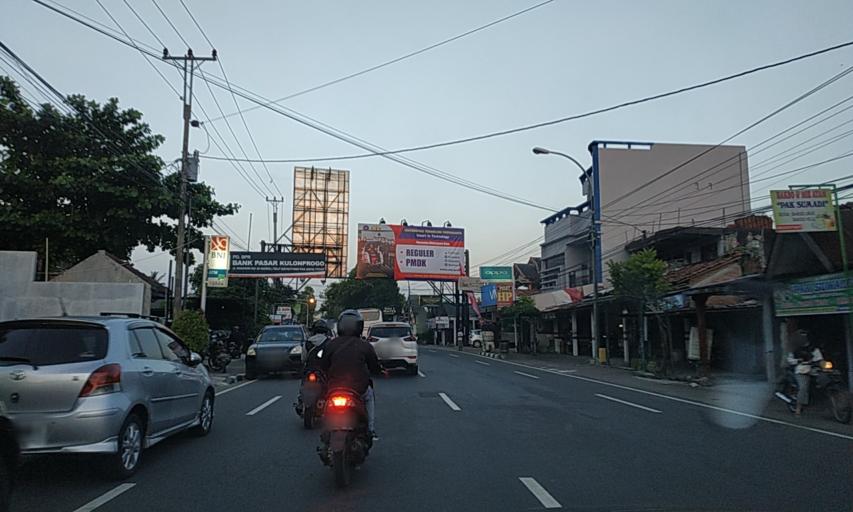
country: ID
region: Daerah Istimewa Yogyakarta
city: Srandakan
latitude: -7.8652
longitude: 110.1538
